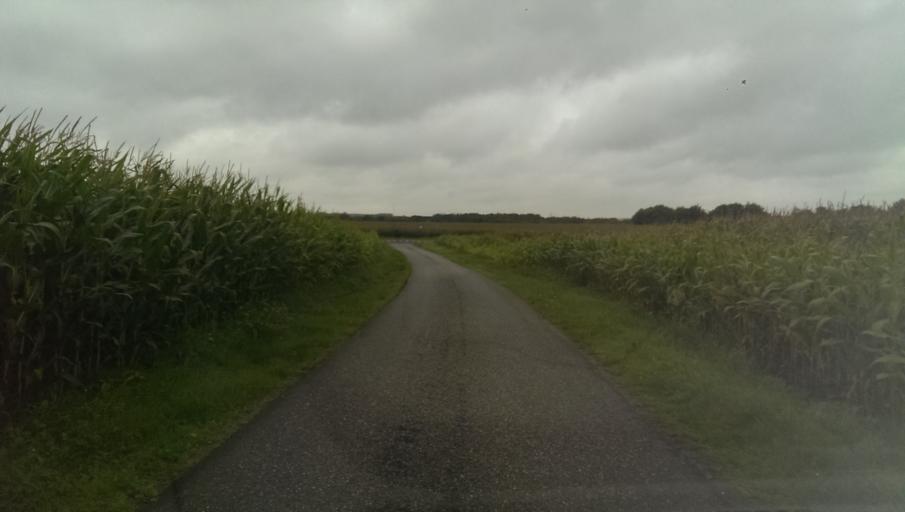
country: DK
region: South Denmark
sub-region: Esbjerg Kommune
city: Tjaereborg
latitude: 55.4929
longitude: 8.6165
